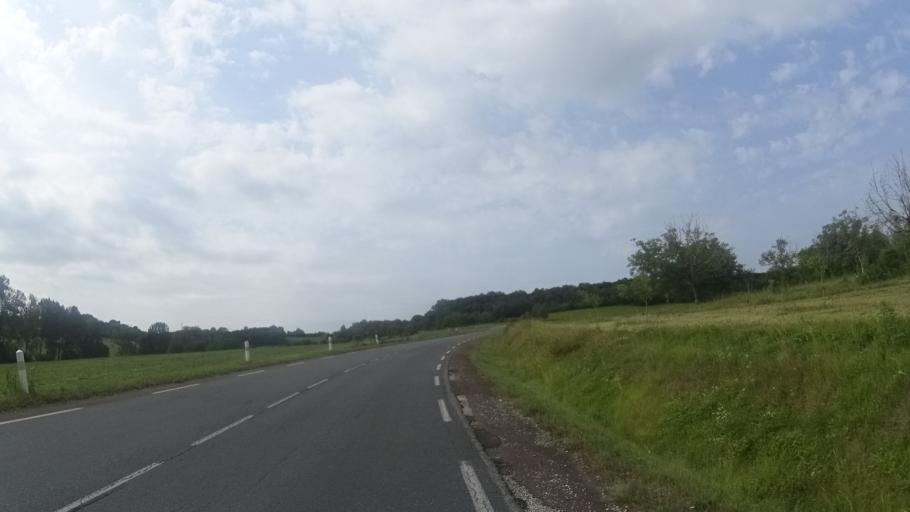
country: FR
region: Aquitaine
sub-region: Departement de la Dordogne
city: Riberac
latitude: 45.2095
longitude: 0.3667
